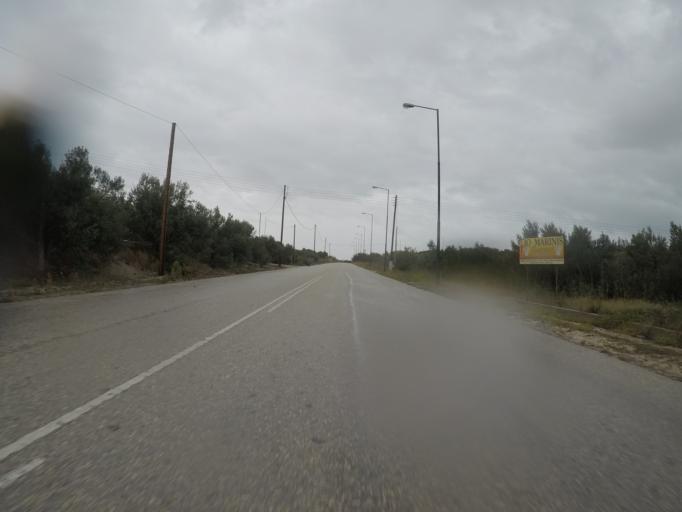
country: GR
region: Peloponnese
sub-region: Nomos Korinthias
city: Arkhaia Korinthos
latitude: 37.8972
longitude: 22.8928
